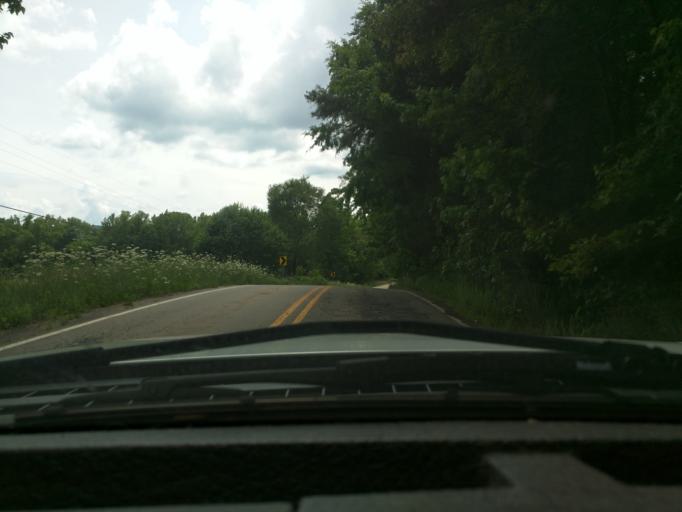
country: US
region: Arkansas
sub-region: Franklin County
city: Ozark
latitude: 35.6852
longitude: -93.8213
